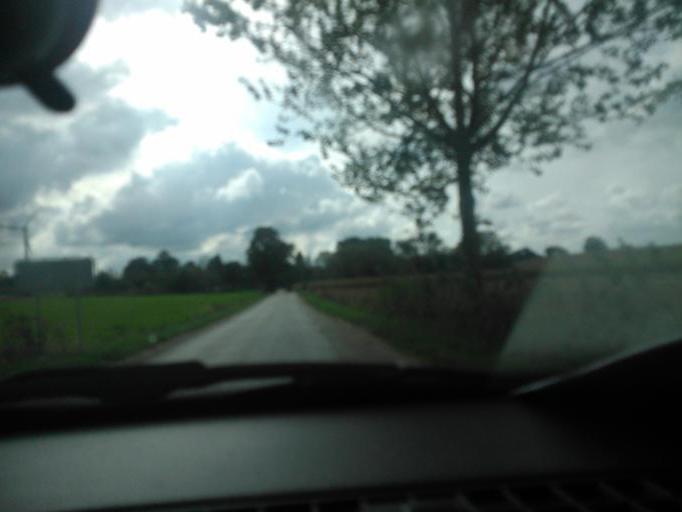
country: PL
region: Kujawsko-Pomorskie
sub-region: Powiat brodnicki
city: Swiedziebnia
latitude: 53.2026
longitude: 19.4758
